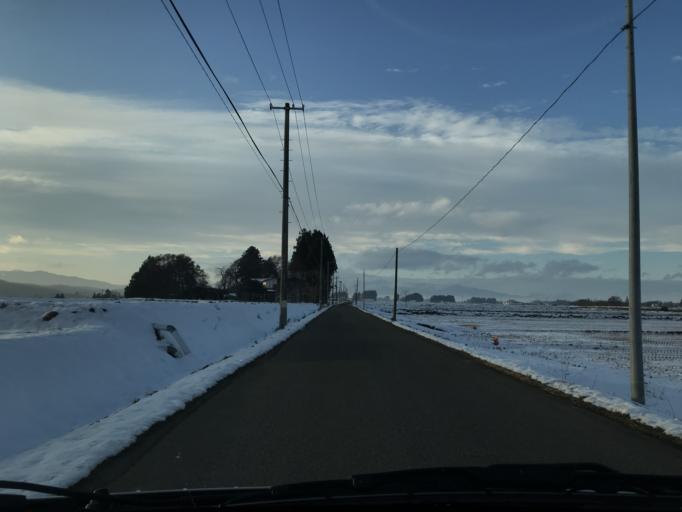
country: JP
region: Iwate
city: Mizusawa
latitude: 39.0491
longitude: 141.1043
